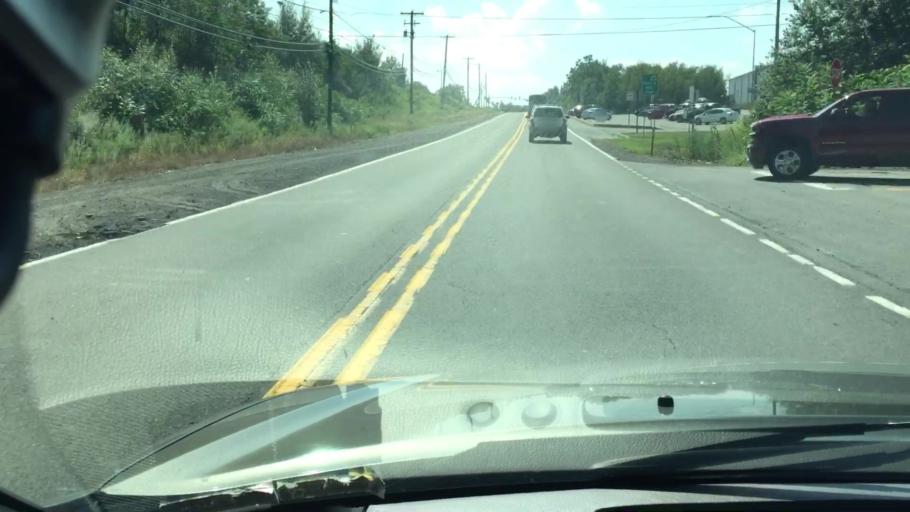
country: US
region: Pennsylvania
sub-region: Luzerne County
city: Ashley
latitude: 41.2021
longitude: -75.9151
